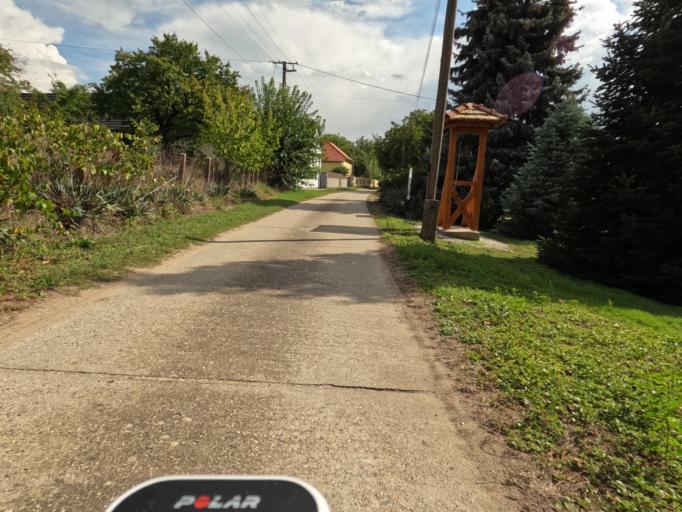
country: HU
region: Tolna
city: Tengelic
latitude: 46.5073
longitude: 18.6900
